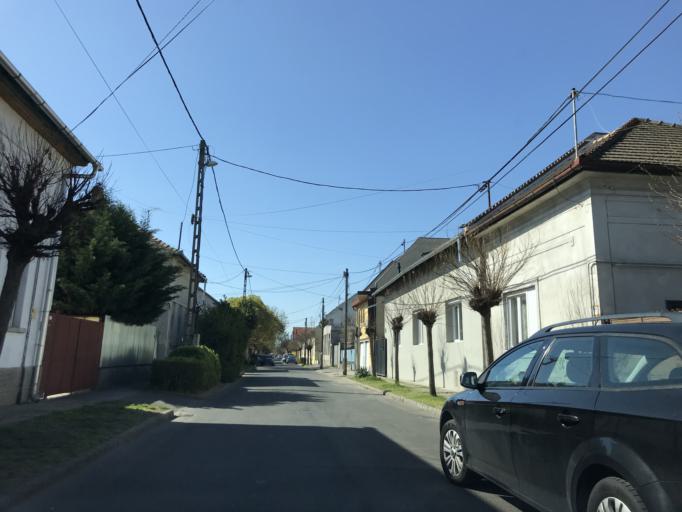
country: HU
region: Budapest
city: Budapest XV. keruelet
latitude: 47.5568
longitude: 19.1165
